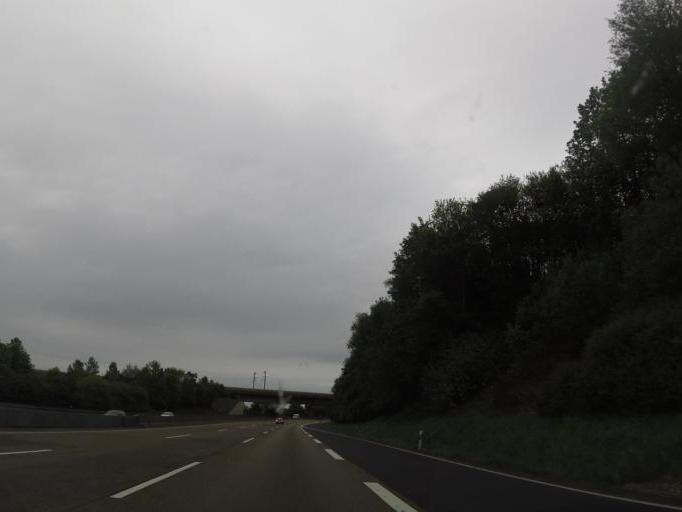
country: DE
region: Hesse
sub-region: Regierungsbezirk Kassel
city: Kirchheim
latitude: 50.9094
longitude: 9.5795
